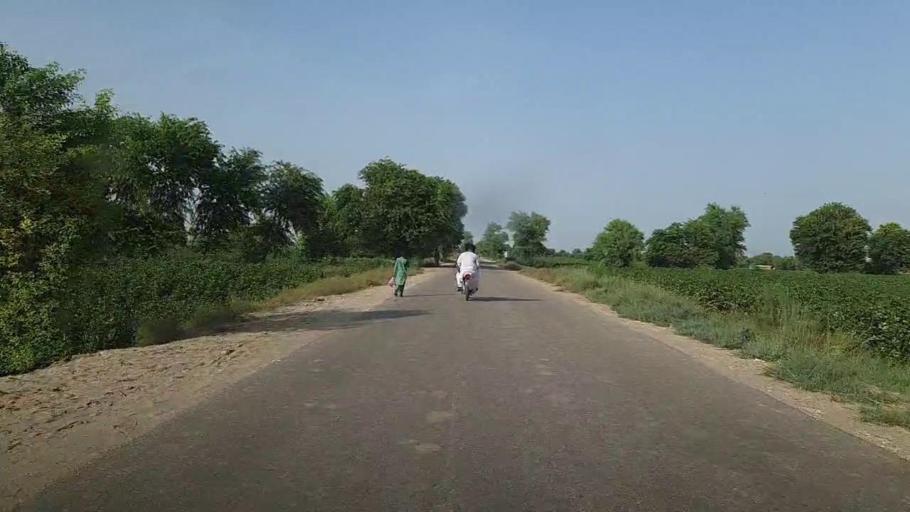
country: PK
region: Sindh
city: Khairpur
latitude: 28.0763
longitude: 69.8300
